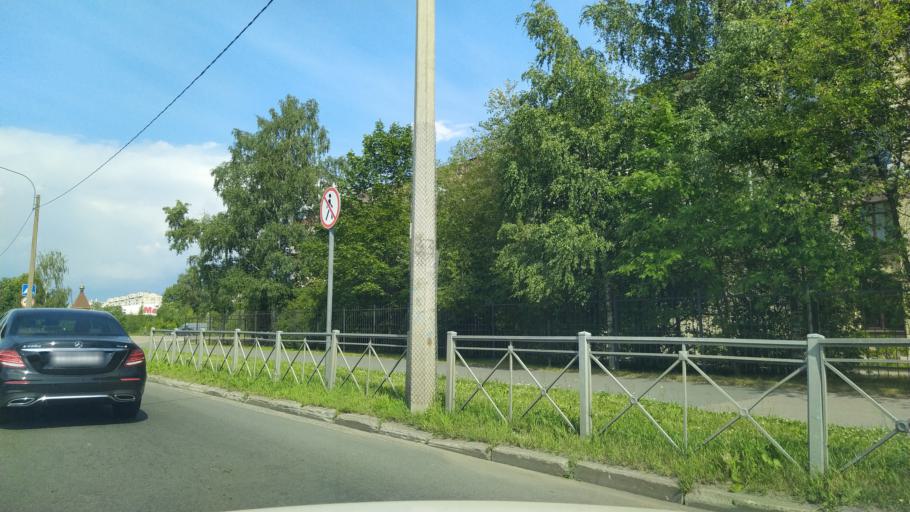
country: RU
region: Leningrad
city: Kalininskiy
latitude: 59.9994
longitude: 30.3789
